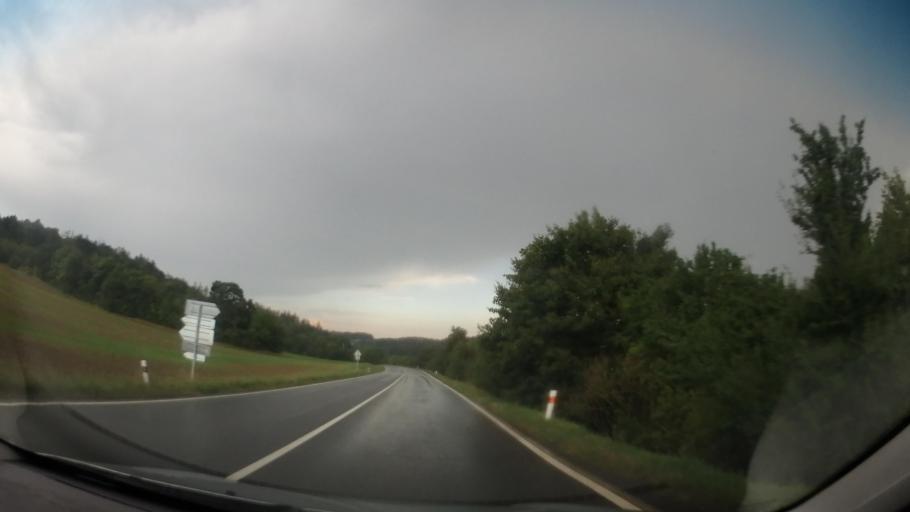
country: CZ
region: Olomoucky
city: Bila Lhota
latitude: 49.7050
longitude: 16.9830
